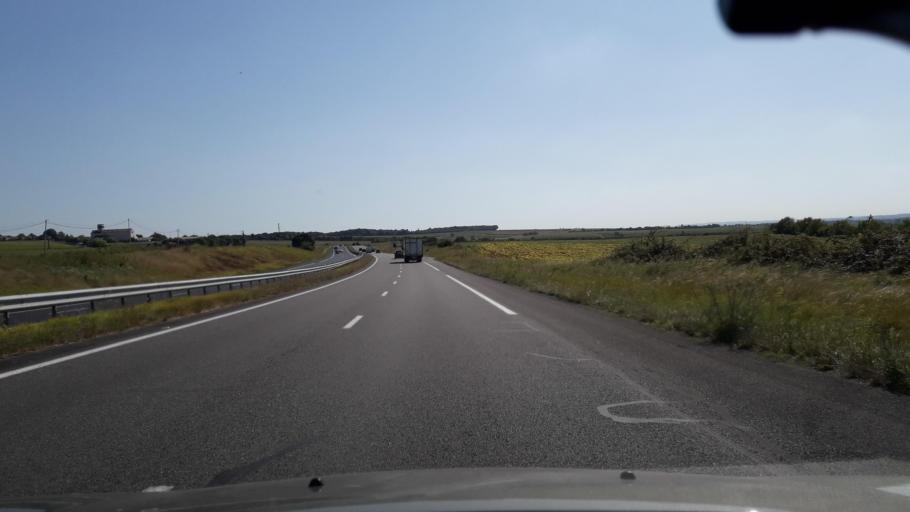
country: FR
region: Poitou-Charentes
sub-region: Departement de la Charente-Maritime
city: Cherac
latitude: 45.6996
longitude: -0.4548
